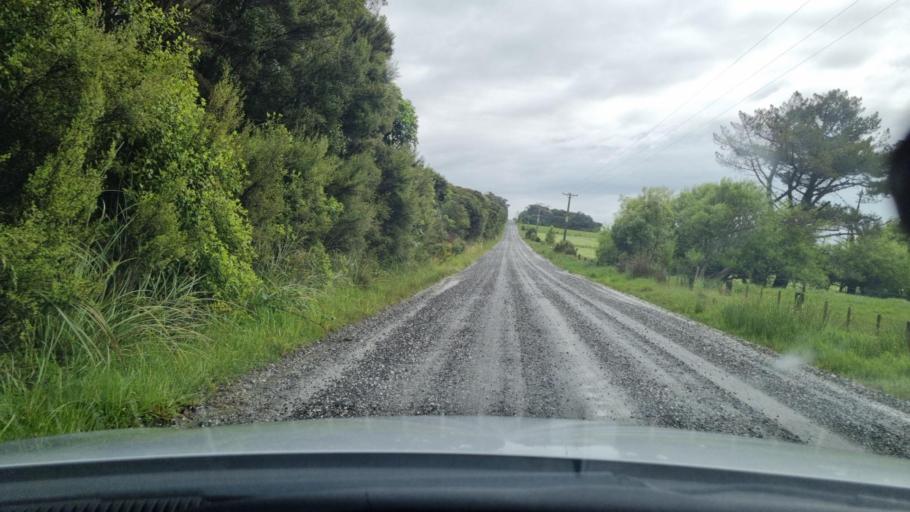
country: NZ
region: Southland
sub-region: Invercargill City
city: Bluff
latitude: -46.5326
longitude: 168.2673
